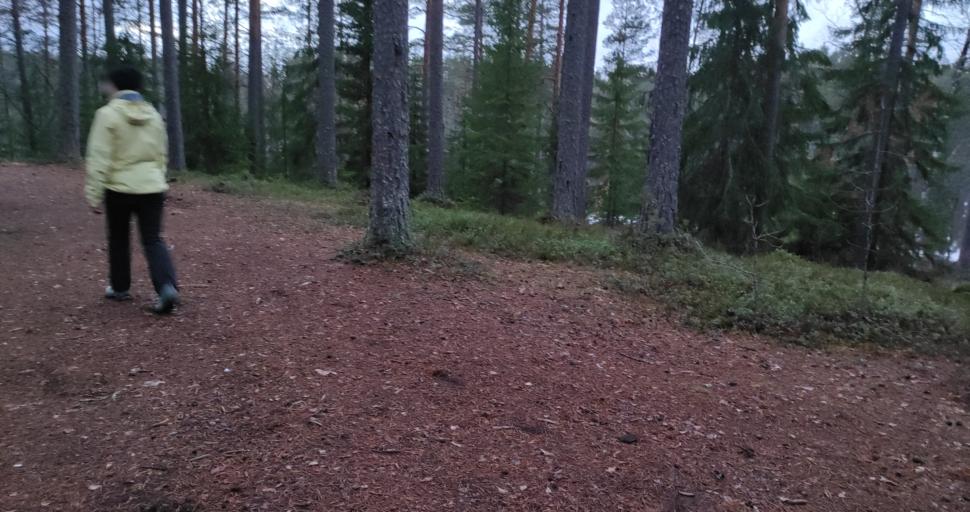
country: RU
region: Leningrad
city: Sosnovo
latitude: 60.5837
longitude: 30.1024
